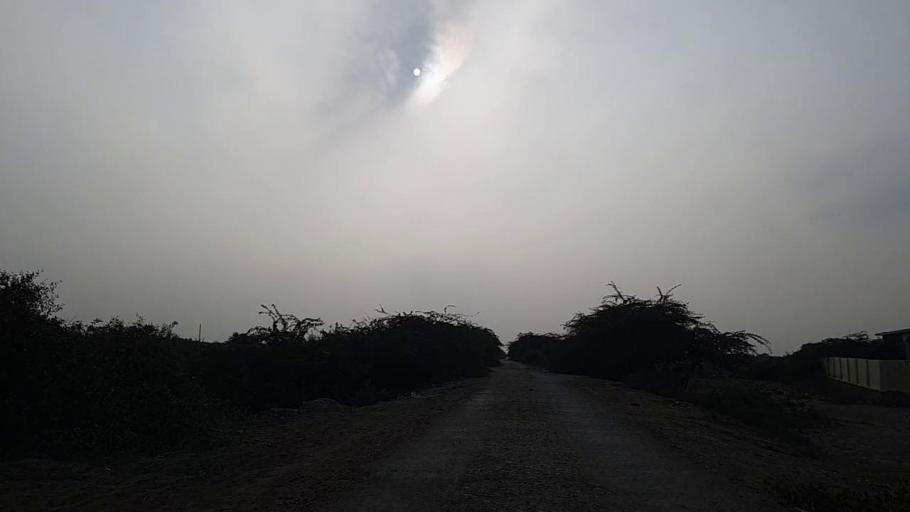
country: PK
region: Sindh
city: Mirpur Sakro
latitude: 24.6106
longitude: 67.5332
